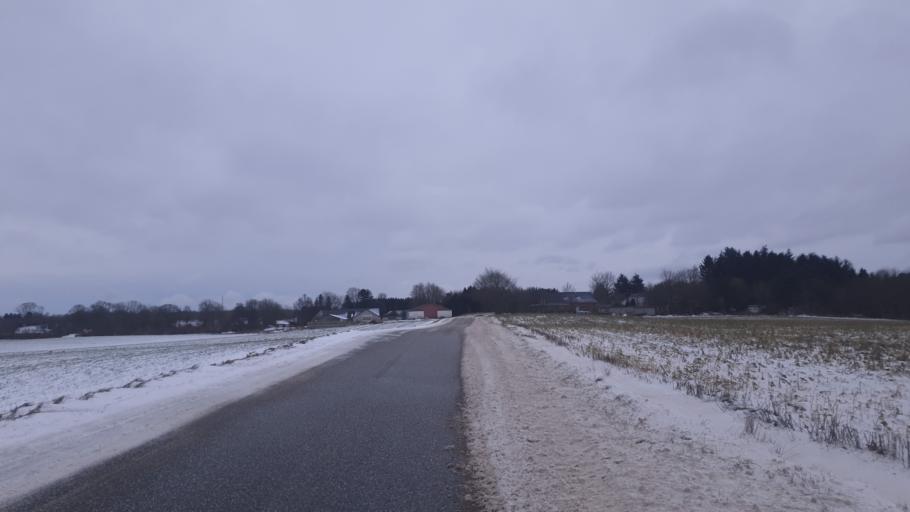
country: DK
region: Central Jutland
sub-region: Hedensted Kommune
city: Hedensted
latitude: 55.7963
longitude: 9.7064
